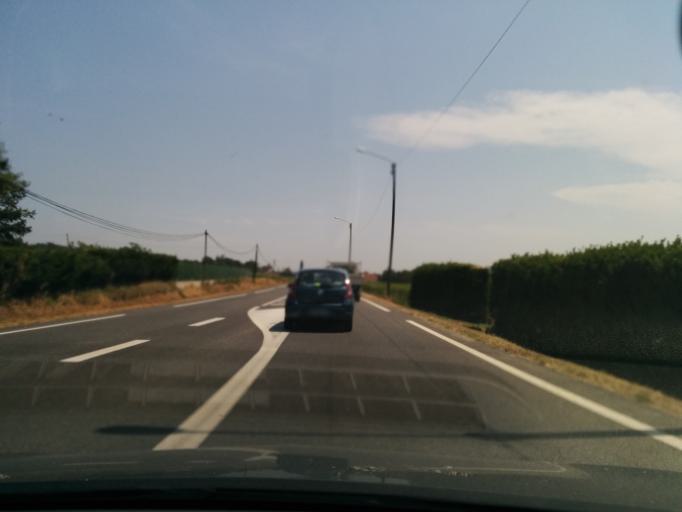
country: FR
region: Midi-Pyrenees
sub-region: Departement de la Haute-Garonne
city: Villefranche-de-Lauragais
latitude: 43.3874
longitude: 1.7295
